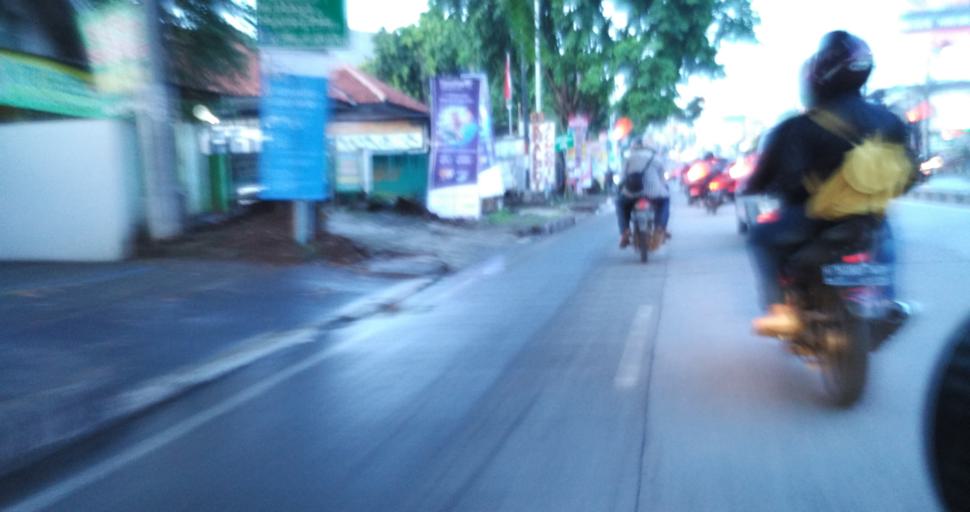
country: ID
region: Central Java
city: Semarang
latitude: -7.0492
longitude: 110.4192
